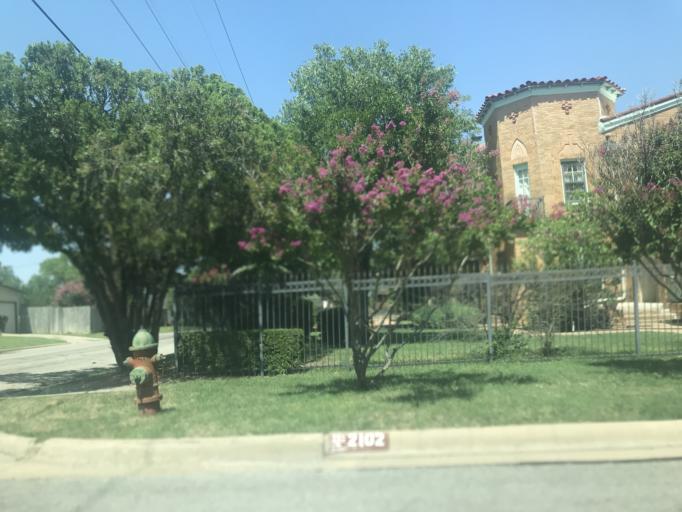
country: US
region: Texas
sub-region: Taylor County
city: Abilene
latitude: 32.4730
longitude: -99.7405
